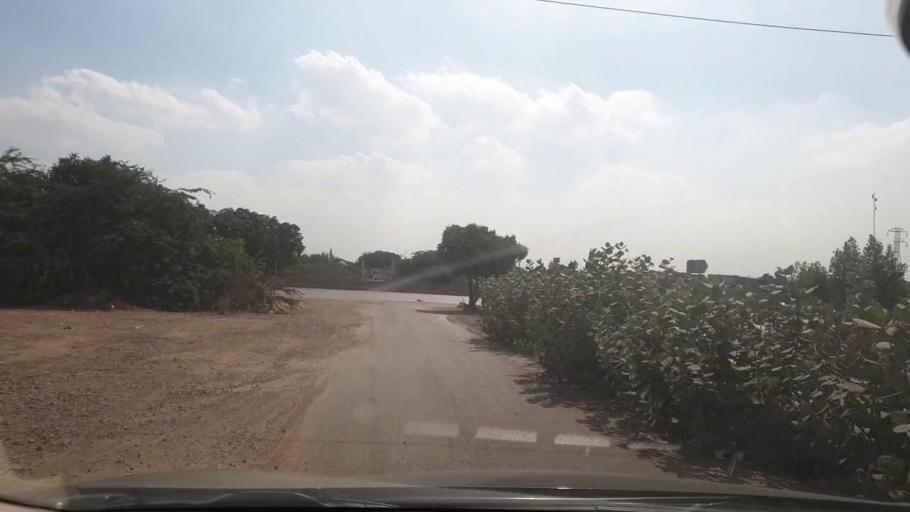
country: PK
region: Sindh
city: Malir Cantonment
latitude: 25.0077
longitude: 67.3563
